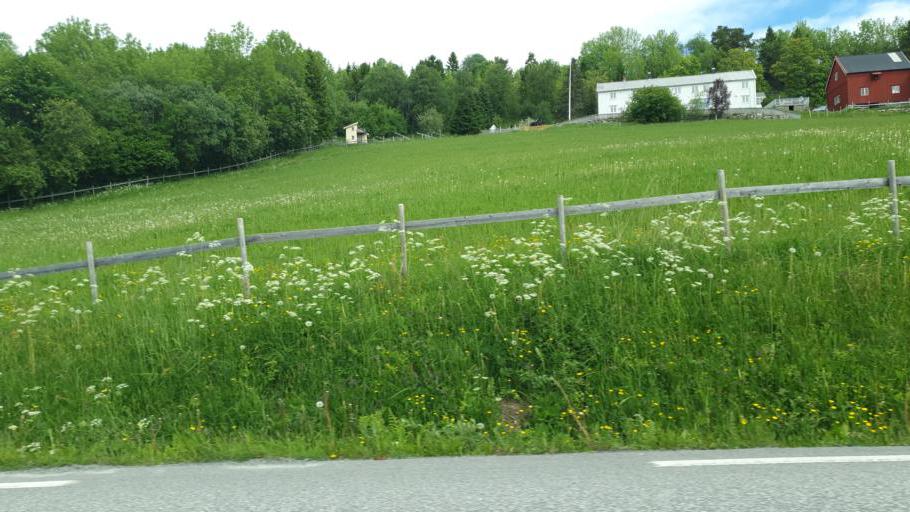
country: NO
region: Sor-Trondelag
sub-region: Trondheim
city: Trondheim
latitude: 63.5736
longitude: 10.3923
